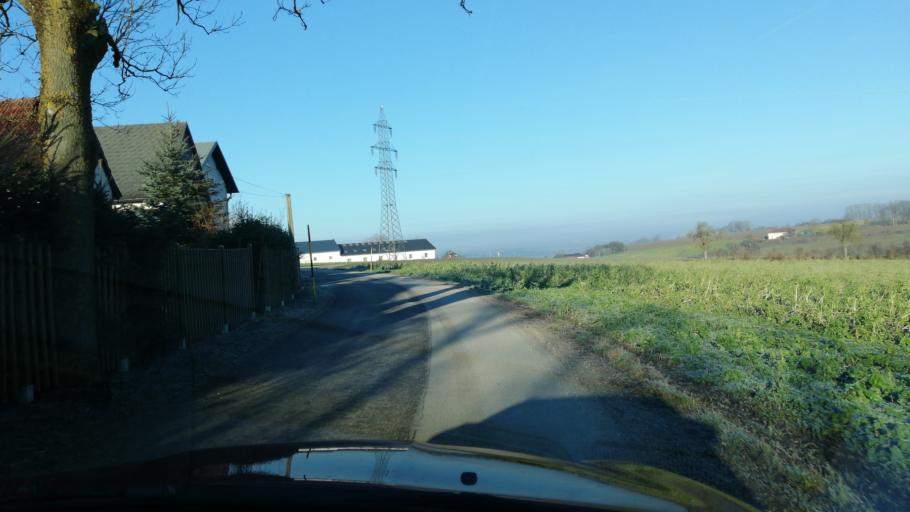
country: AT
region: Upper Austria
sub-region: Politischer Bezirk Steyr-Land
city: Bad Hall
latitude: 48.0516
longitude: 14.2162
